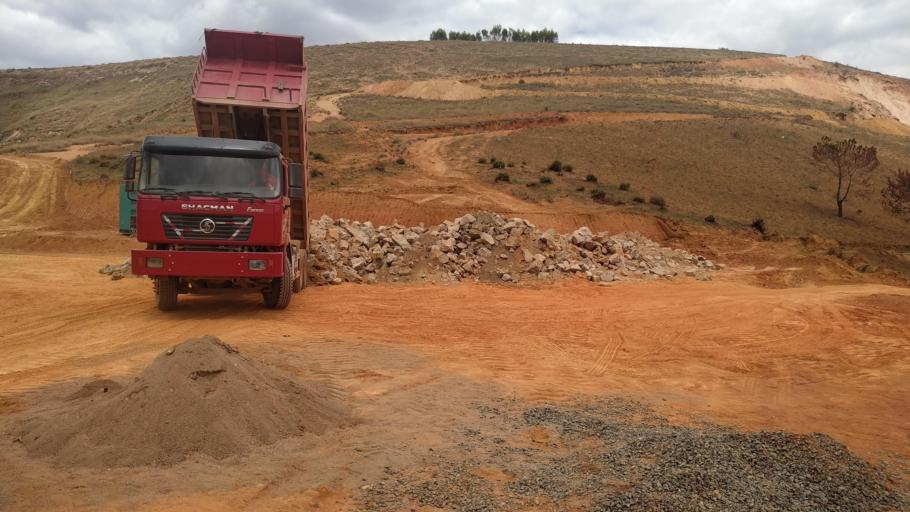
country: MG
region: Alaotra Mangoro
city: Ambatondrazaka
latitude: -17.8840
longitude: 48.2931
